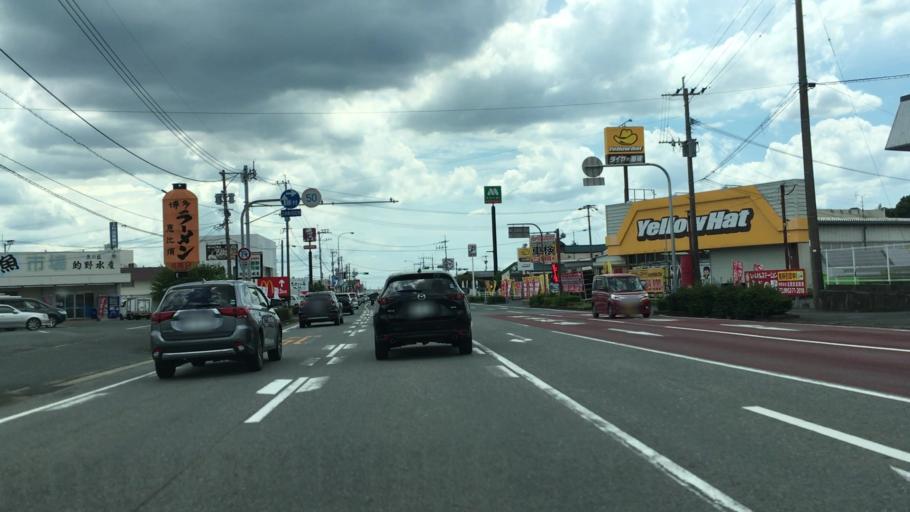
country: JP
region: Saga Prefecture
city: Tosu
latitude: 33.3890
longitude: 130.5000
